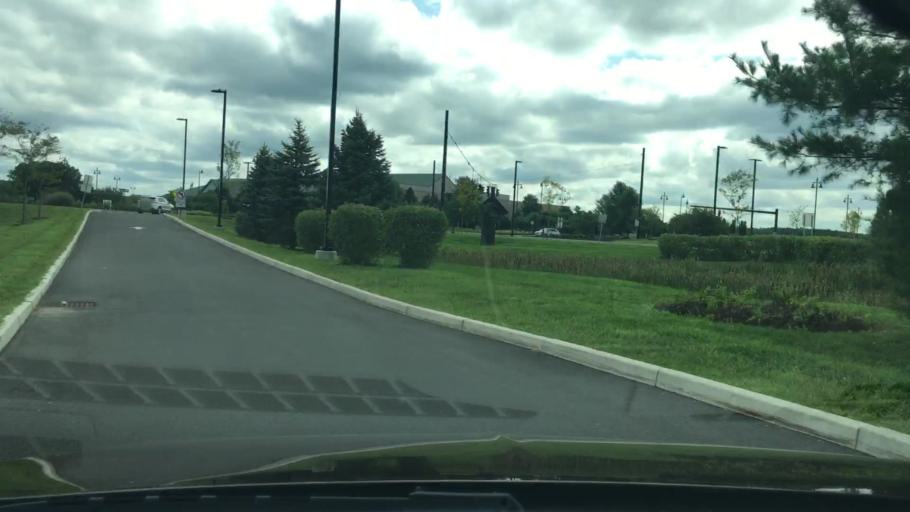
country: US
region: Connecticut
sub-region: Hartford County
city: East Hartford
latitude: 41.7558
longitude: -72.6262
